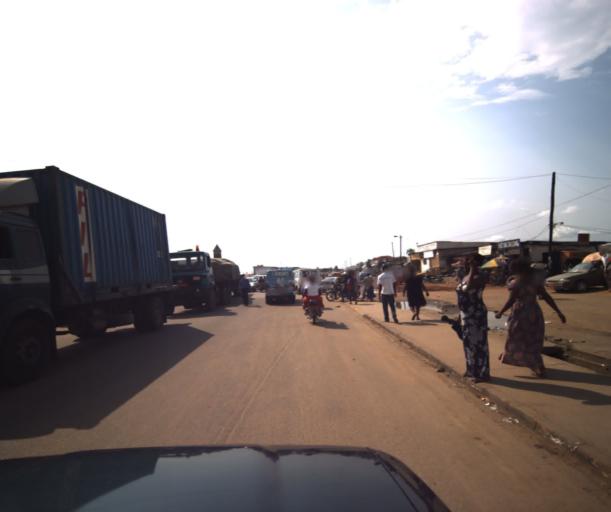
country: CM
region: Littoral
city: Douala
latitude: 4.0120
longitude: 9.7320
